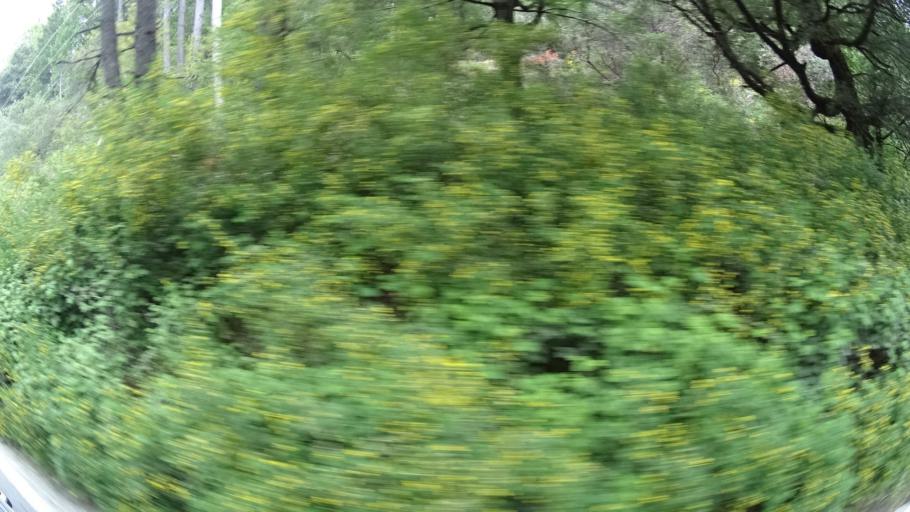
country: US
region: California
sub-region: Humboldt County
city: Redway
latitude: 40.1146
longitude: -123.8867
